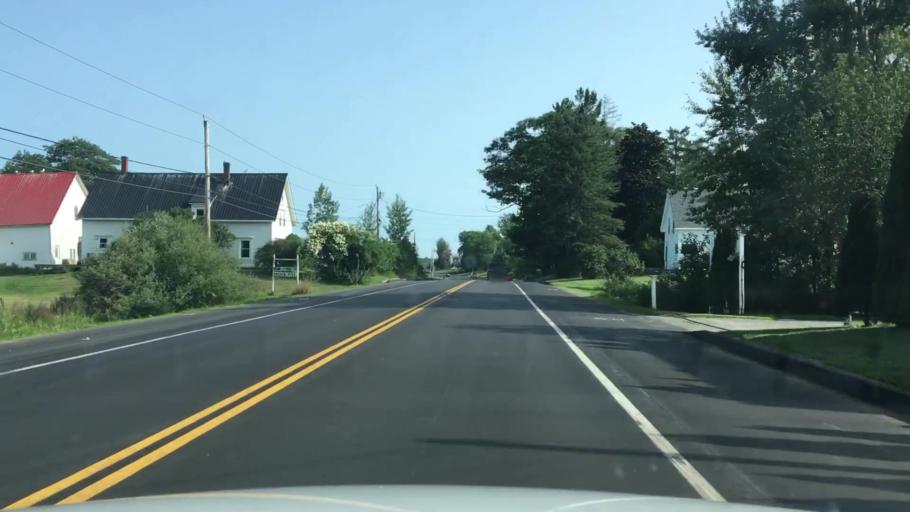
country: US
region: Maine
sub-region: Knox County
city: Warren
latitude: 44.1082
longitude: -69.2528
